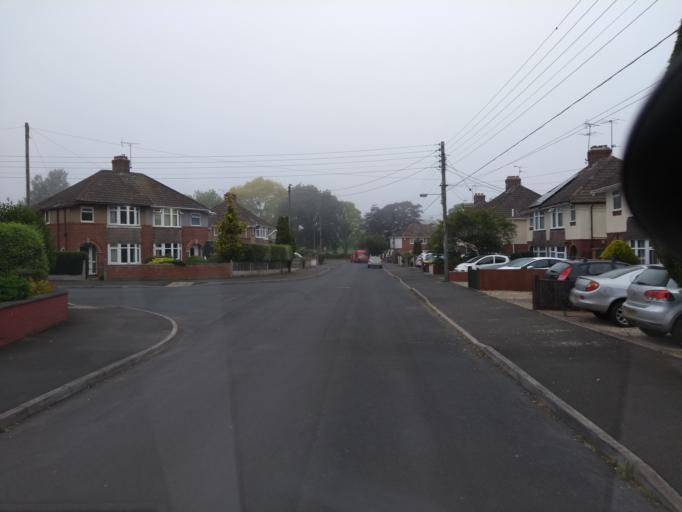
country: GB
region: England
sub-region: Somerset
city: Taunton
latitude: 51.0259
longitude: -3.0936
